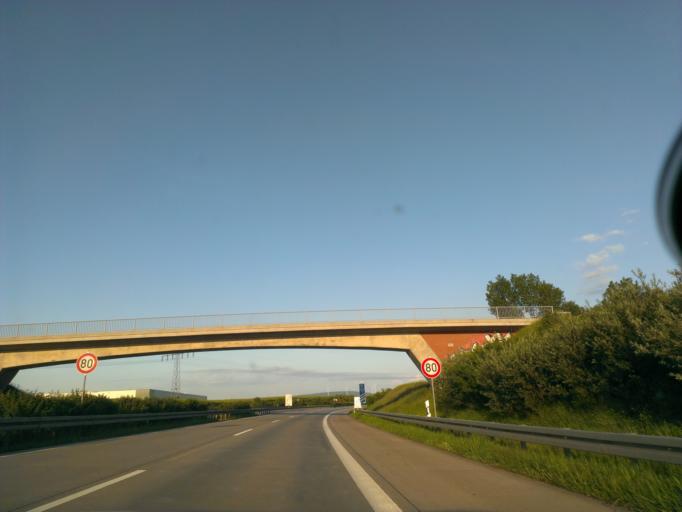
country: DE
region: Thuringia
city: Noda
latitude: 51.0400
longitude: 11.0282
